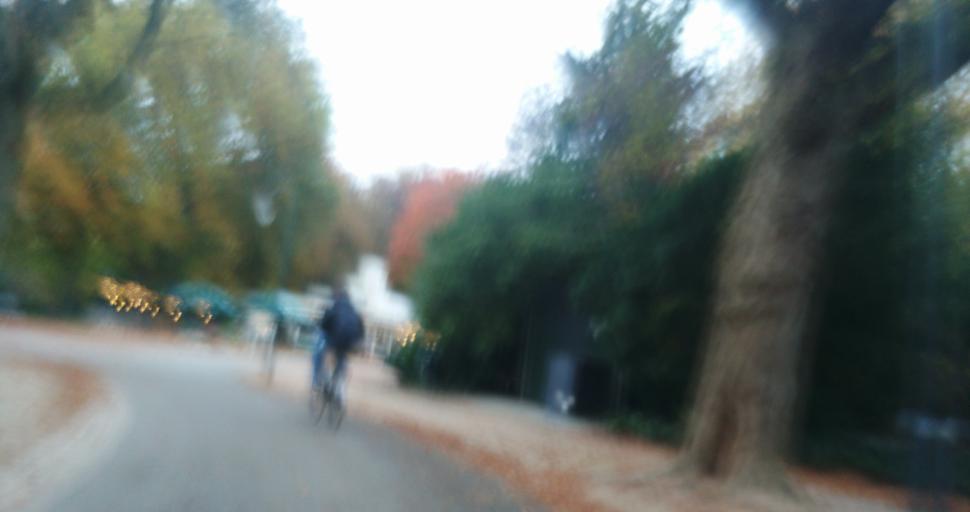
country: NL
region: Groningen
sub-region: Gemeente Groningen
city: Groningen
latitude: 53.2239
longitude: 6.5560
